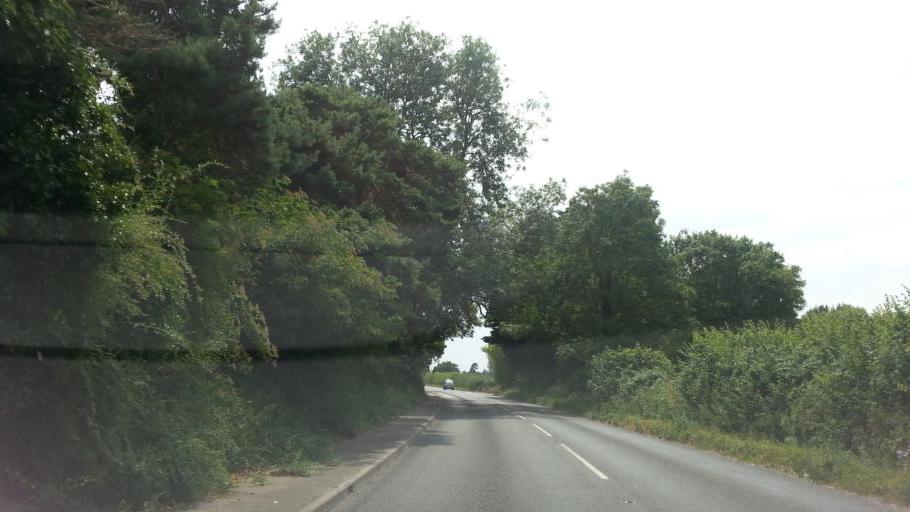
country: GB
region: England
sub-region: Suffolk
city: Lakenheath
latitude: 52.3886
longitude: 0.5283
